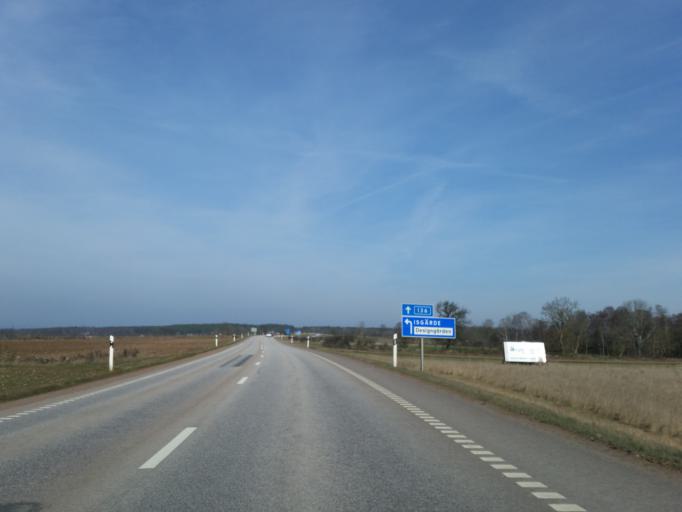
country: SE
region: Kalmar
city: Faerjestaden
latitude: 56.7266
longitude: 16.5386
